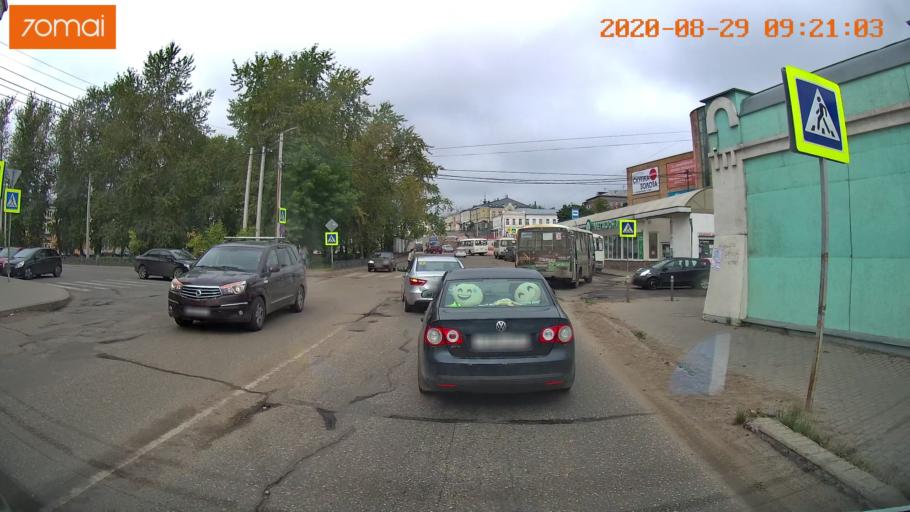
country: RU
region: Ivanovo
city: Kineshma
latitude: 57.4422
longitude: 42.1714
